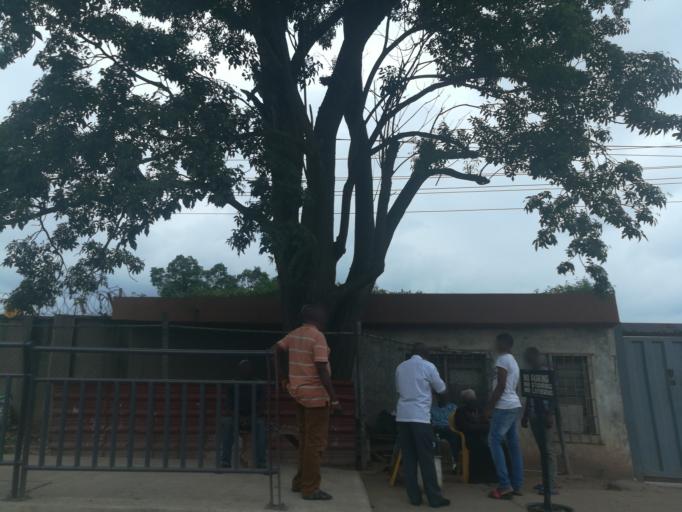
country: NG
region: Lagos
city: Ikeja
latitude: 6.6087
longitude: 3.3559
